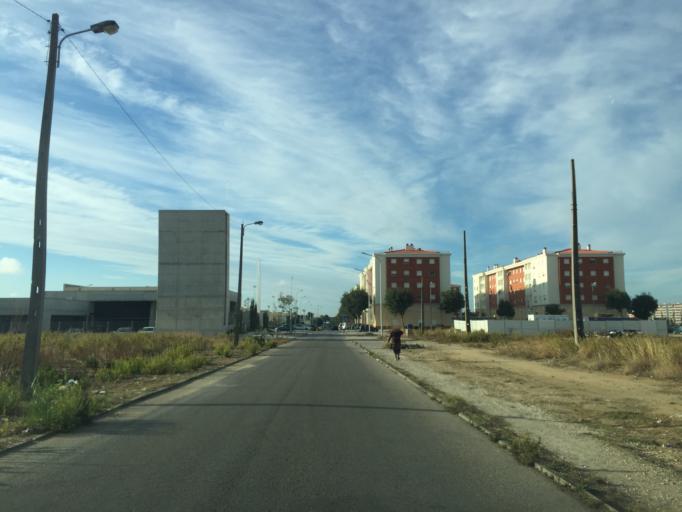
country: PT
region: Lisbon
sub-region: Odivelas
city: Olival do Basto
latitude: 38.7801
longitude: -9.1439
